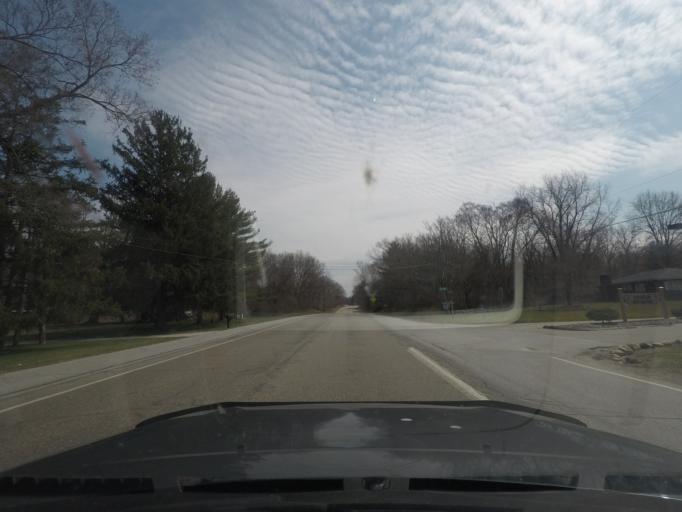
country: US
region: Indiana
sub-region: LaPorte County
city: Trail Creek
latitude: 41.6870
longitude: -86.7981
